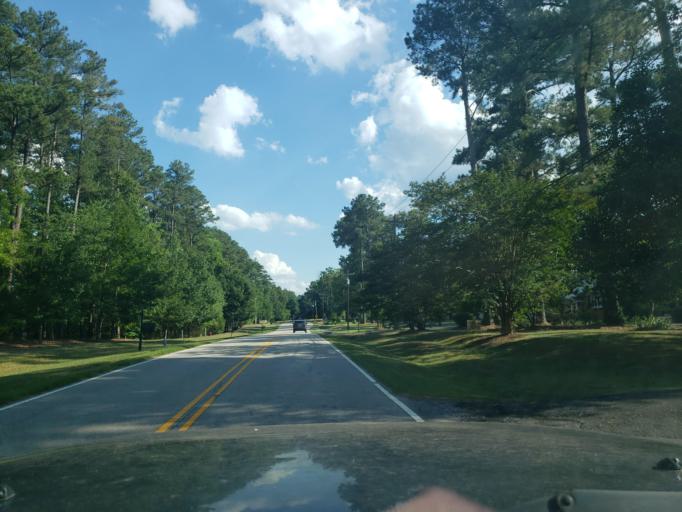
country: US
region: North Carolina
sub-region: Durham County
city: Durham
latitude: 35.9807
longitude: -78.9899
